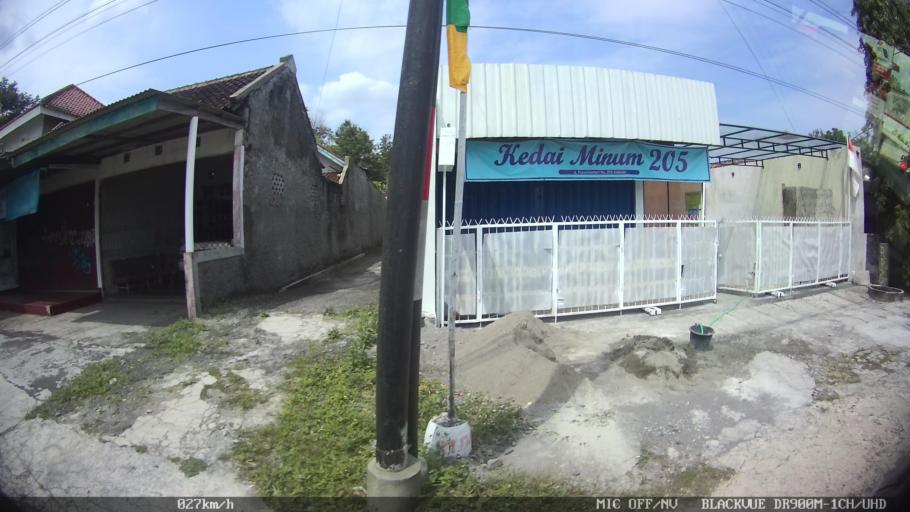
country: ID
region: Daerah Istimewa Yogyakarta
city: Depok
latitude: -7.7328
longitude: 110.4514
